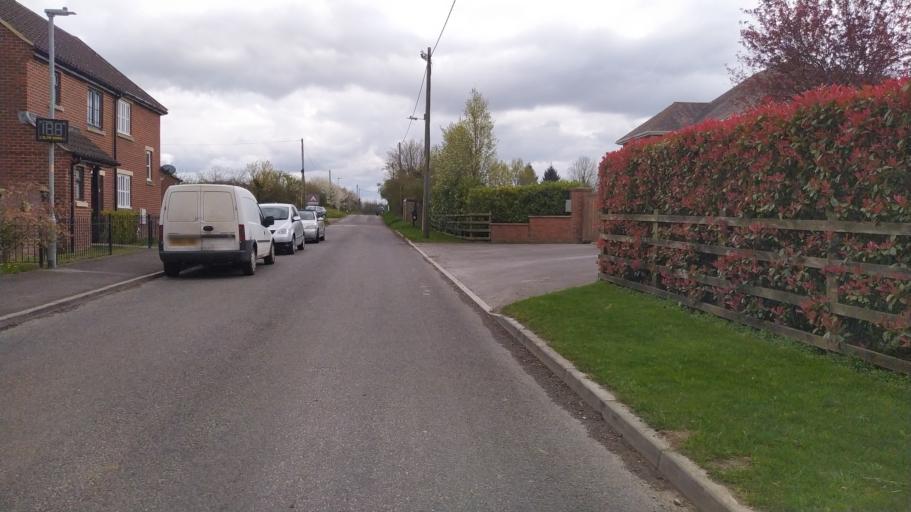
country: GB
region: England
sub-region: Wiltshire
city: North Bradley
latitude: 51.2960
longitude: -2.1714
